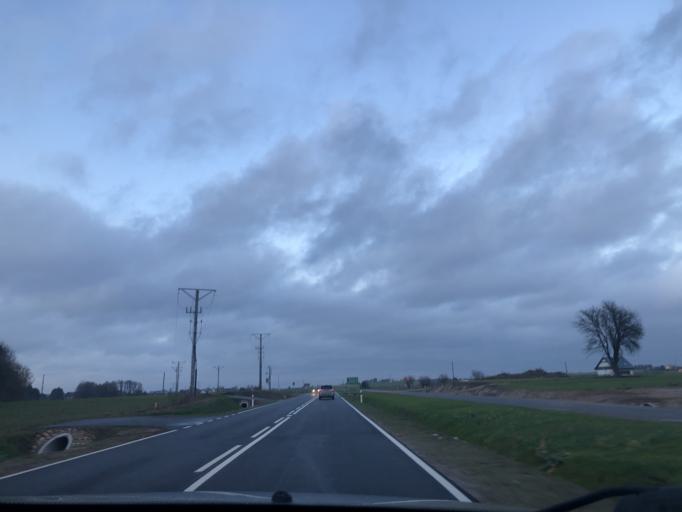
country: PL
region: Podlasie
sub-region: Lomza
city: Lomza
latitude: 53.1357
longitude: 22.0503
